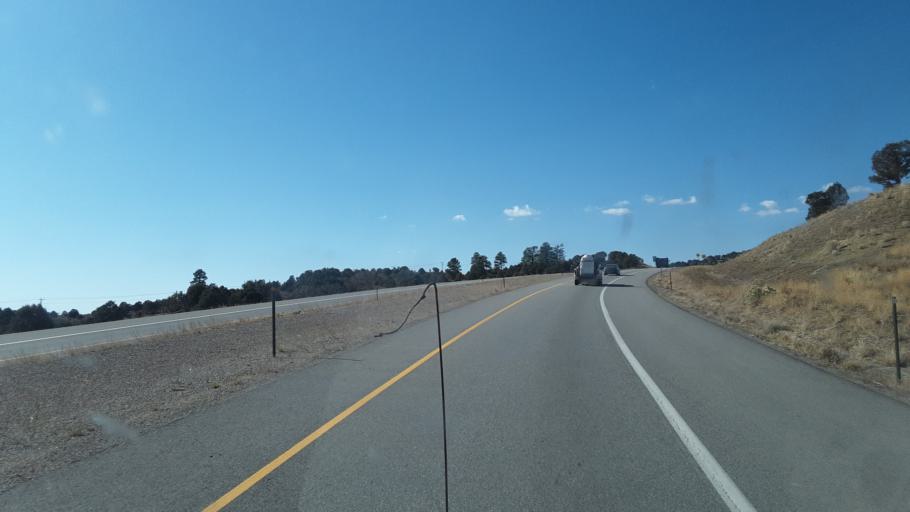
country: US
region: Colorado
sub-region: La Plata County
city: Bayfield
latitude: 37.2257
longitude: -107.6905
